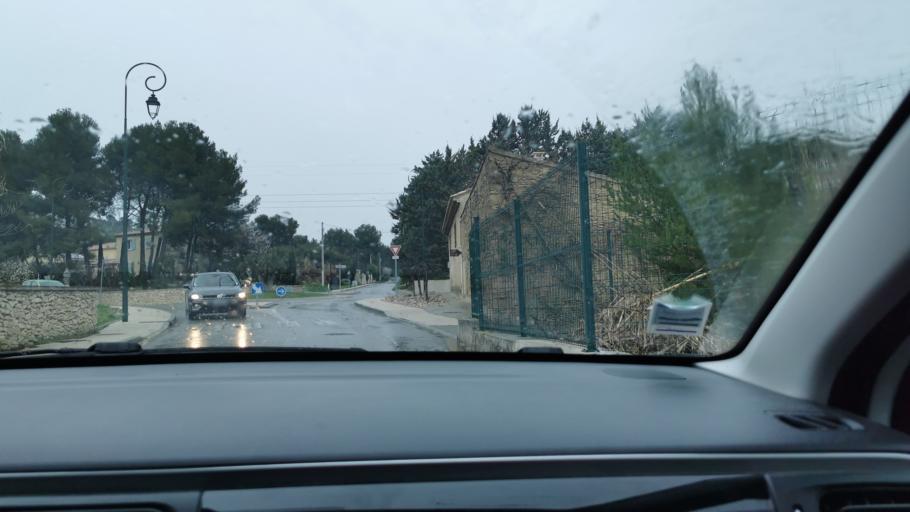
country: FR
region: Provence-Alpes-Cote d'Azur
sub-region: Departement des Bouches-du-Rhone
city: Eyguieres
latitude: 43.7000
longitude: 5.0360
